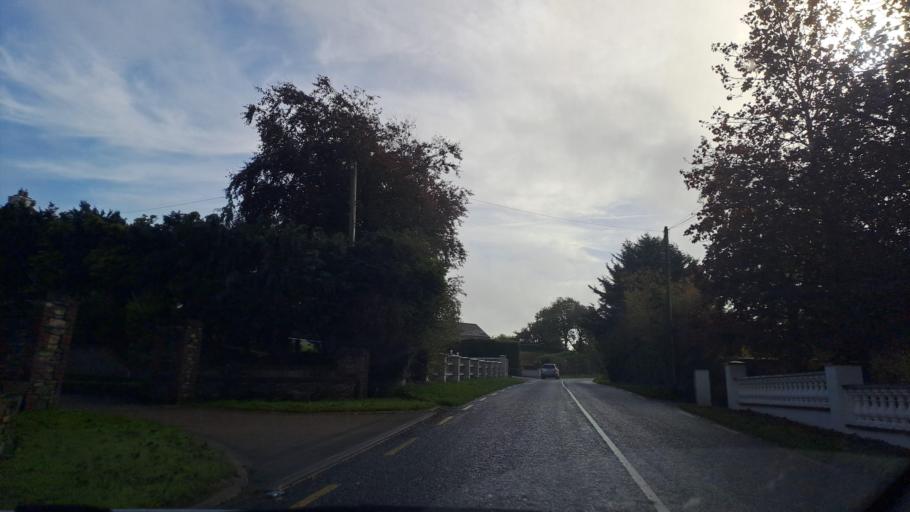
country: IE
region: Ulster
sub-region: County Monaghan
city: Carrickmacross
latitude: 53.9575
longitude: -6.7116
